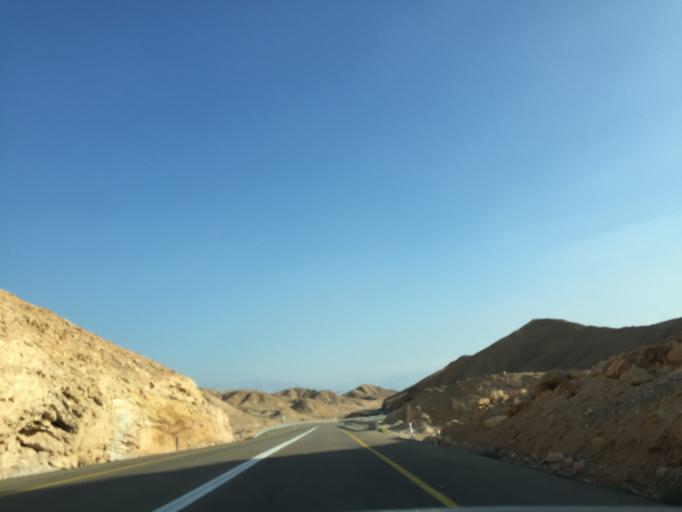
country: IL
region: Southern District
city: `En Boqeq
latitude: 31.1903
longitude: 35.2838
